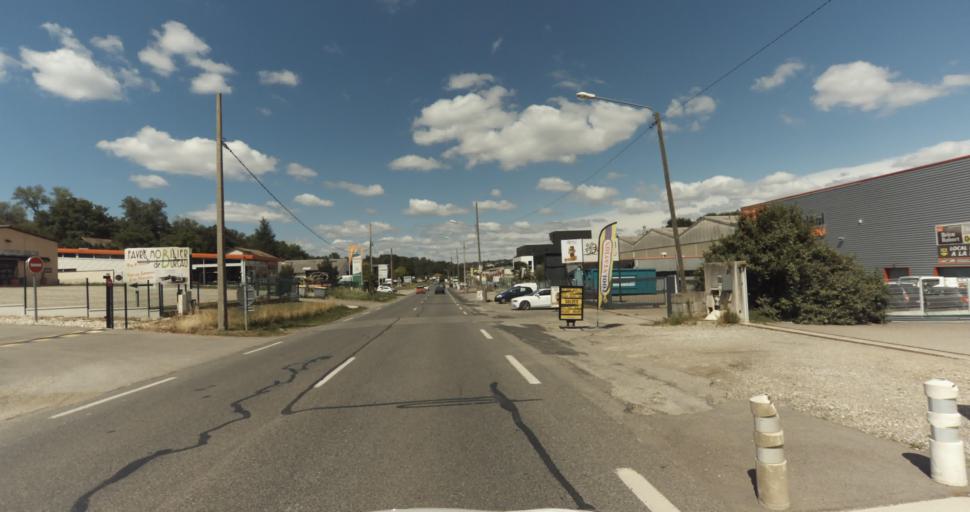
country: FR
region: Rhone-Alpes
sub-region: Departement du Rhone
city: Chaponost
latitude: 45.7093
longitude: 4.7701
